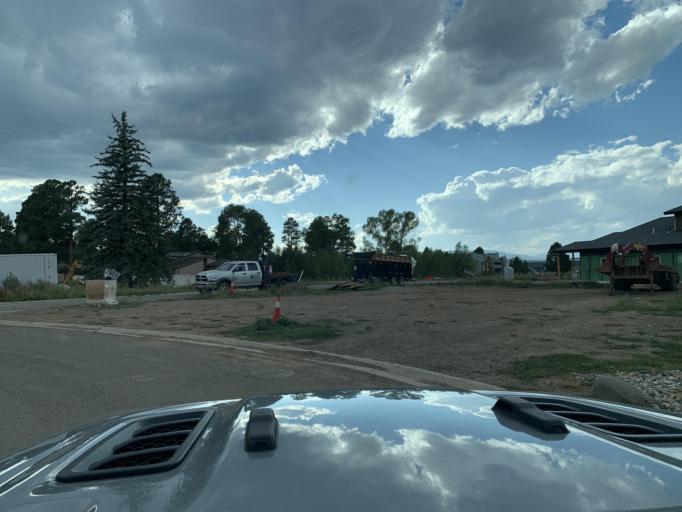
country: US
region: Colorado
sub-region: Archuleta County
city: Pagosa Springs
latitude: 37.2613
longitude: -107.0680
